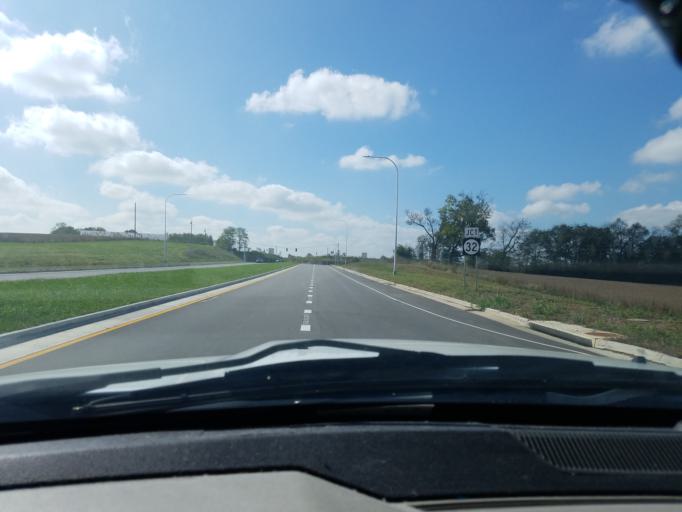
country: US
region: Kentucky
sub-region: Scott County
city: Georgetown
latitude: 38.2401
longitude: -84.5509
